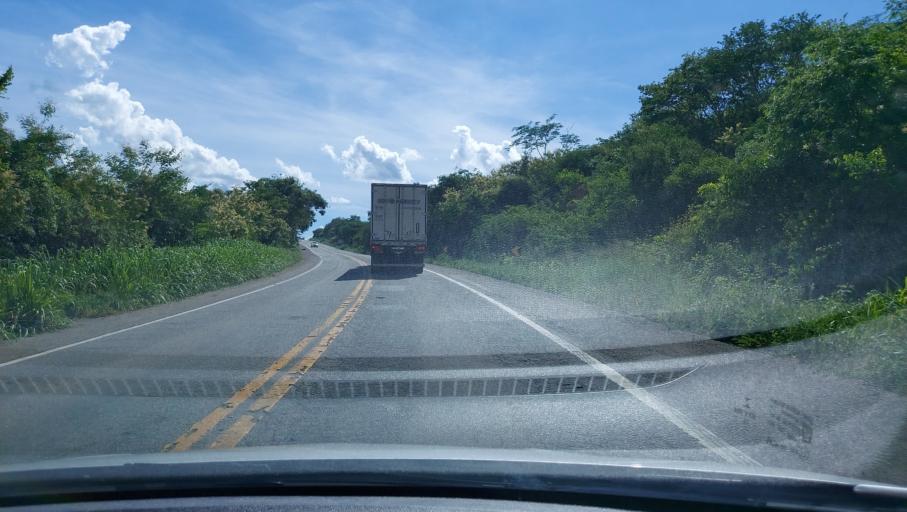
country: BR
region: Bahia
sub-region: Andarai
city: Vera Cruz
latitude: -12.4678
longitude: -41.0942
